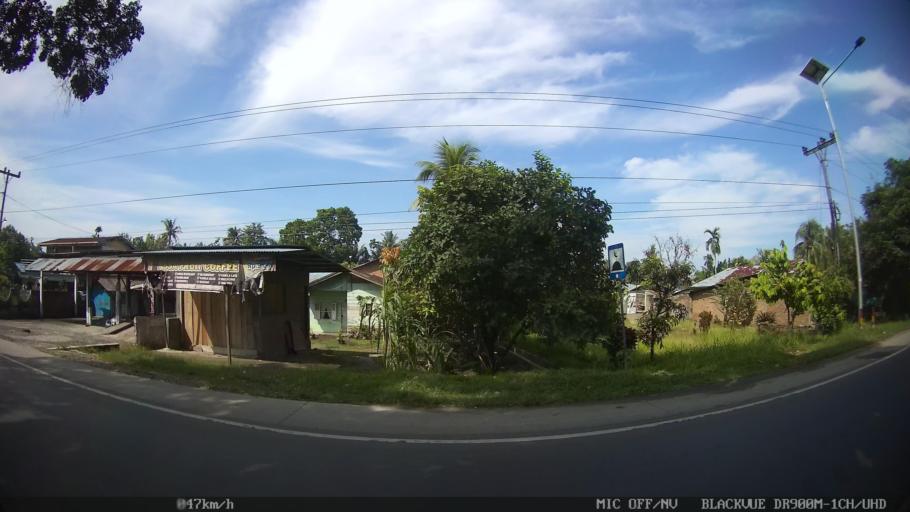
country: ID
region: North Sumatra
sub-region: Kabupaten Langkat
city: Stabat
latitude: 3.7222
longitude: 98.5018
